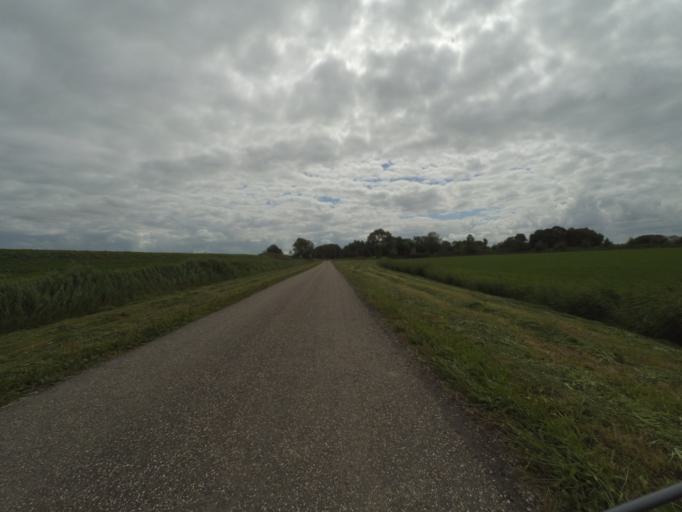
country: NL
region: Friesland
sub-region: Gemeente Dongeradeel
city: Anjum
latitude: 53.3330
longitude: 6.1541
